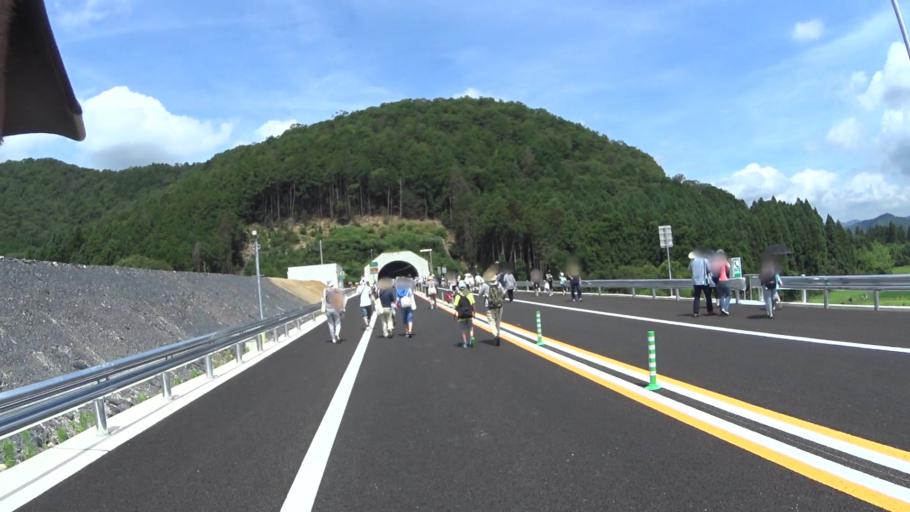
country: JP
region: Hyogo
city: Sasayama
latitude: 35.1580
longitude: 135.4069
